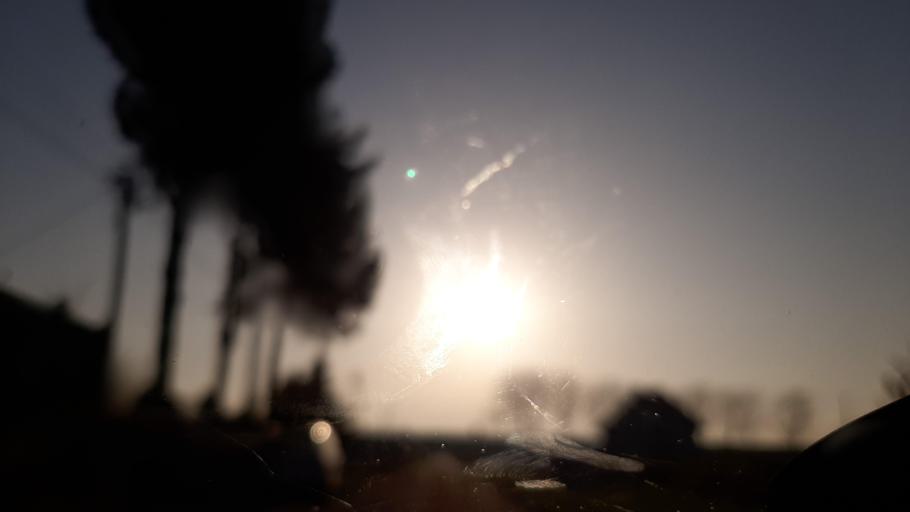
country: PL
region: Lublin Voivodeship
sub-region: Powiat lubelski
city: Garbow
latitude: 51.3725
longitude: 22.3486
